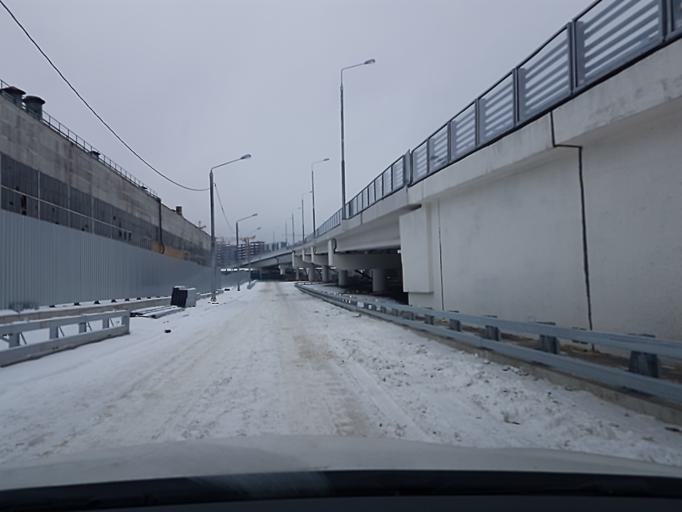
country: RU
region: Moskovskaya
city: Kozhukhovo
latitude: 55.6965
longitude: 37.6512
